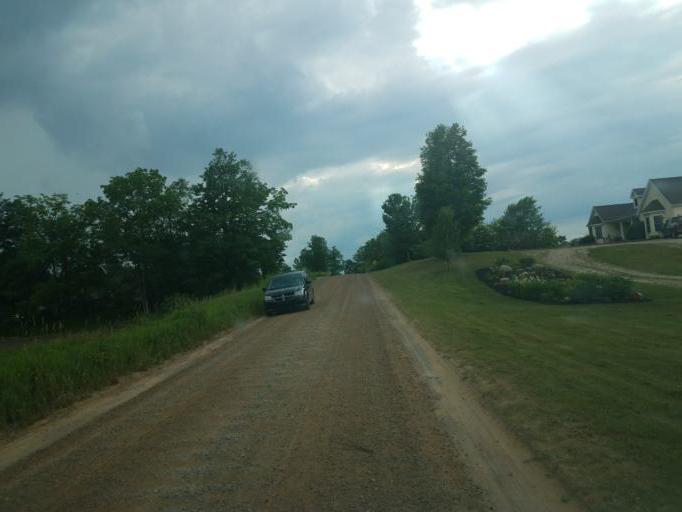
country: US
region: Michigan
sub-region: Barry County
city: Nashville
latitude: 42.5967
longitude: -85.0111
